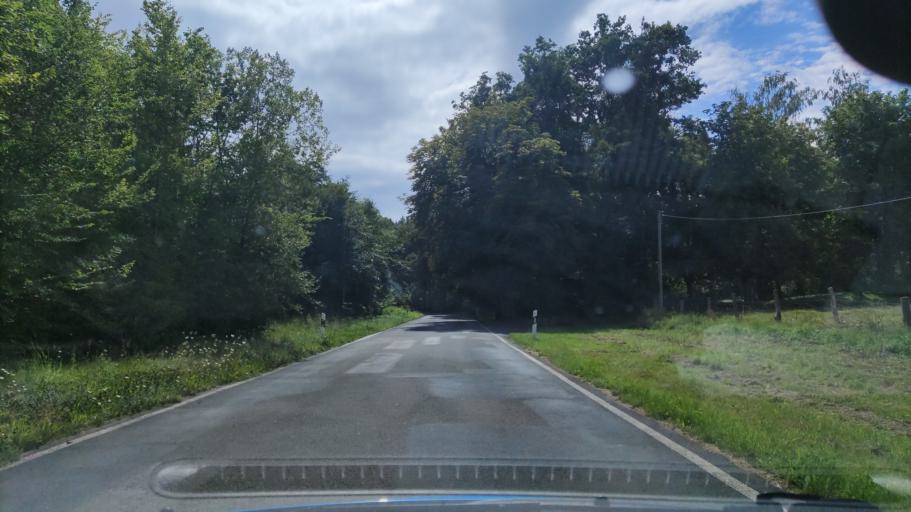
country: DE
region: Lower Saxony
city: Coppengrave
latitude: 51.9663
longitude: 9.7642
